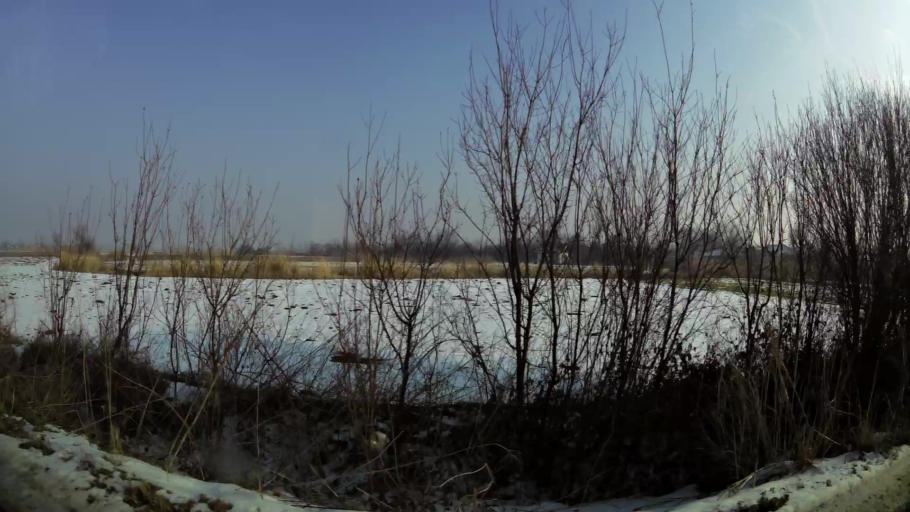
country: MK
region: Petrovec
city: Petrovec
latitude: 41.9479
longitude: 21.5965
